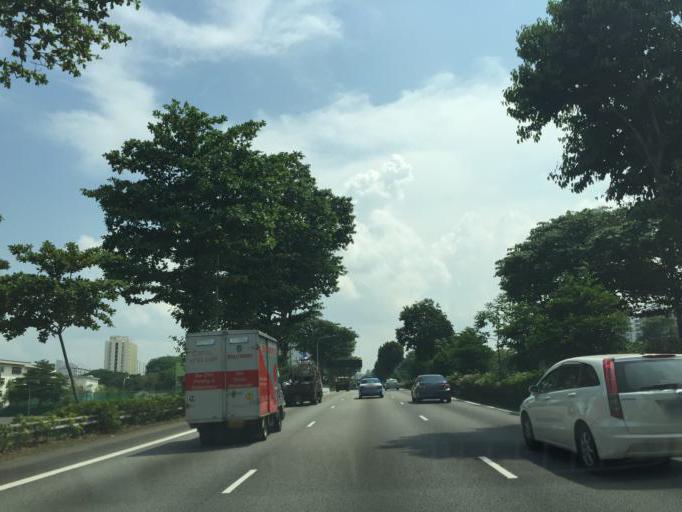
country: SG
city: Singapore
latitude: 1.3352
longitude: 103.9348
